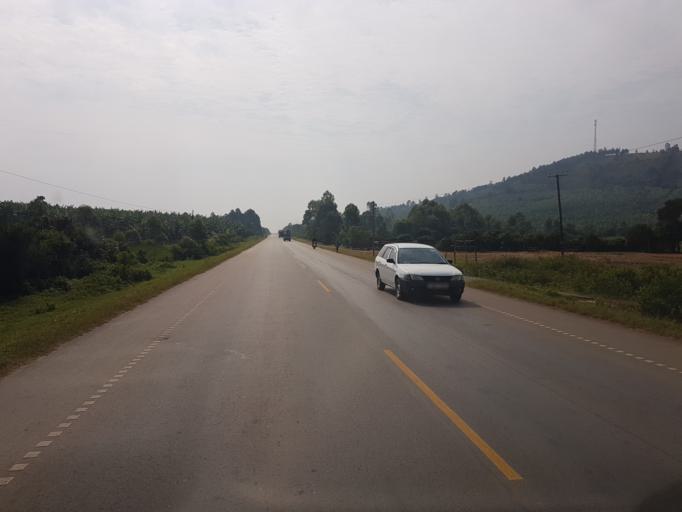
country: UG
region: Western Region
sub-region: Sheema District
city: Kibingo
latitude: -0.6405
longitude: 30.5072
